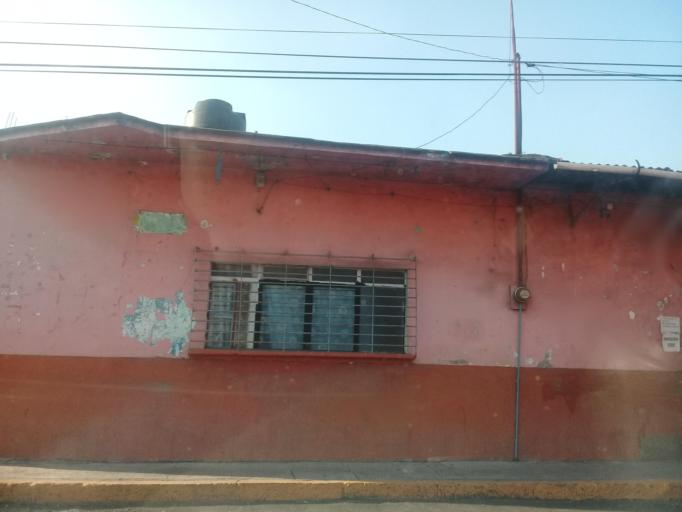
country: MX
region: Veracruz
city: Orizaba
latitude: 18.8561
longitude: -97.1110
